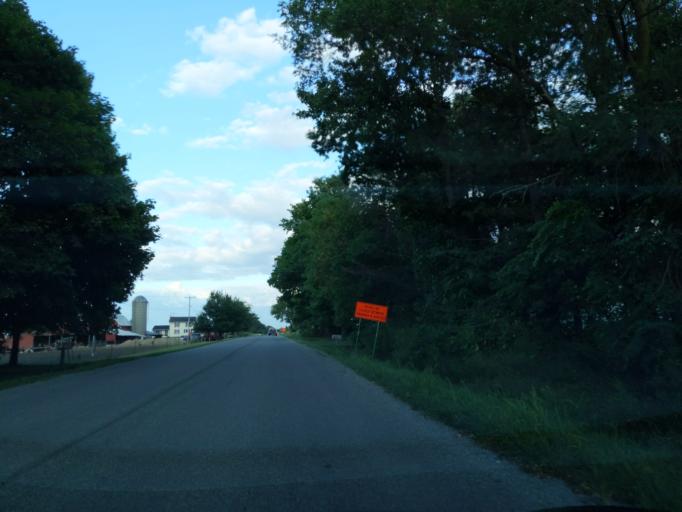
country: US
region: Michigan
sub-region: Ingham County
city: Holt
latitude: 42.5968
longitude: -84.5718
